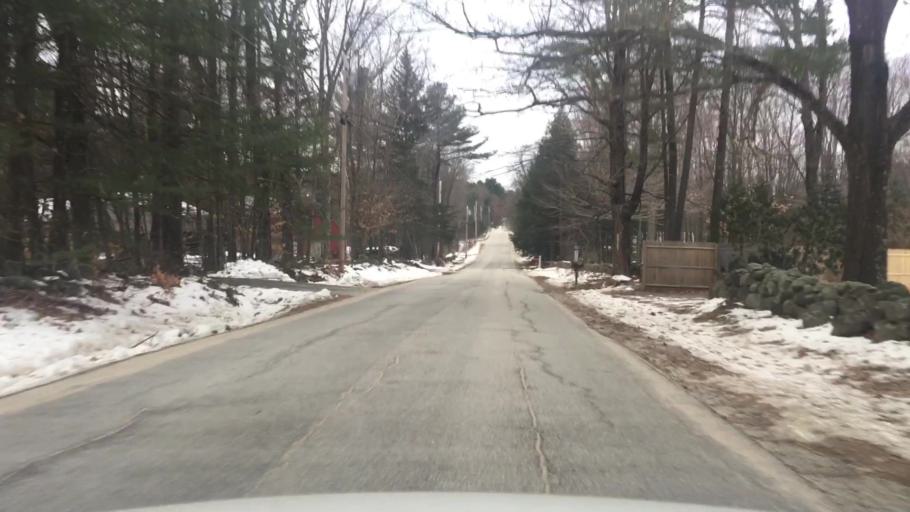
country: US
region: New Hampshire
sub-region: Merrimack County
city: Hopkinton
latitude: 43.1803
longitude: -71.6746
